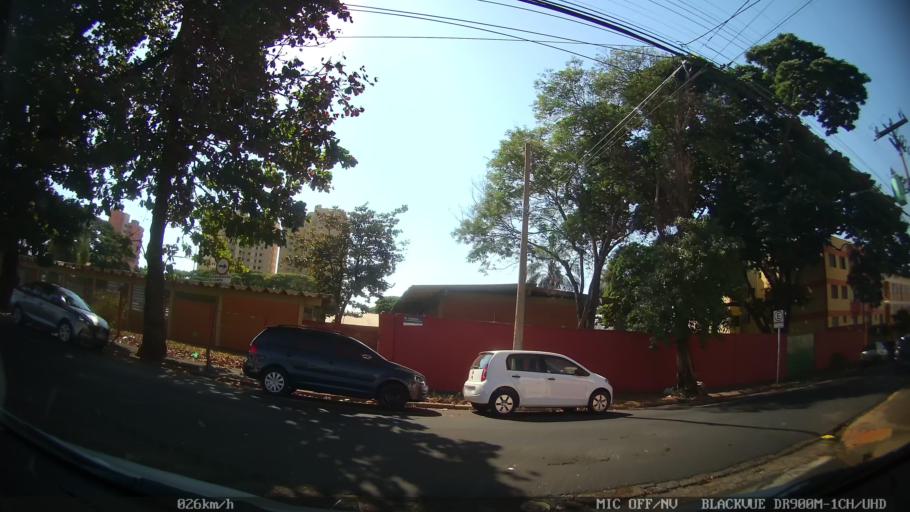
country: BR
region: Sao Paulo
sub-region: Ribeirao Preto
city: Ribeirao Preto
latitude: -21.1898
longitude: -47.8024
